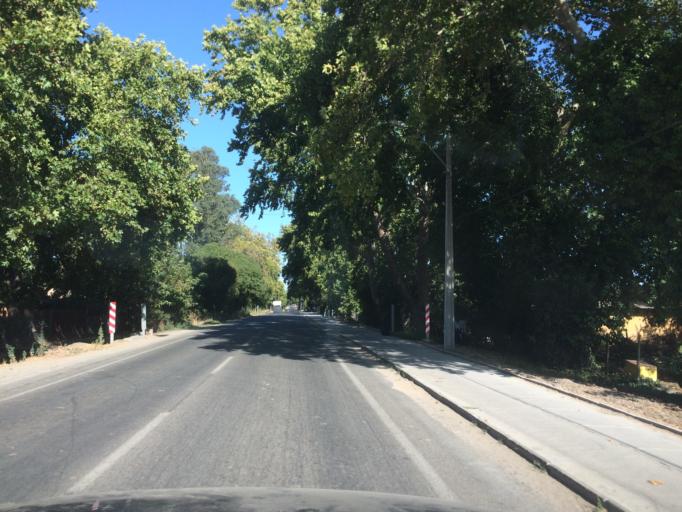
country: CL
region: Santiago Metropolitan
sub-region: Provincia de Melipilla
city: Melipilla
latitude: -33.4922
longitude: -71.1653
